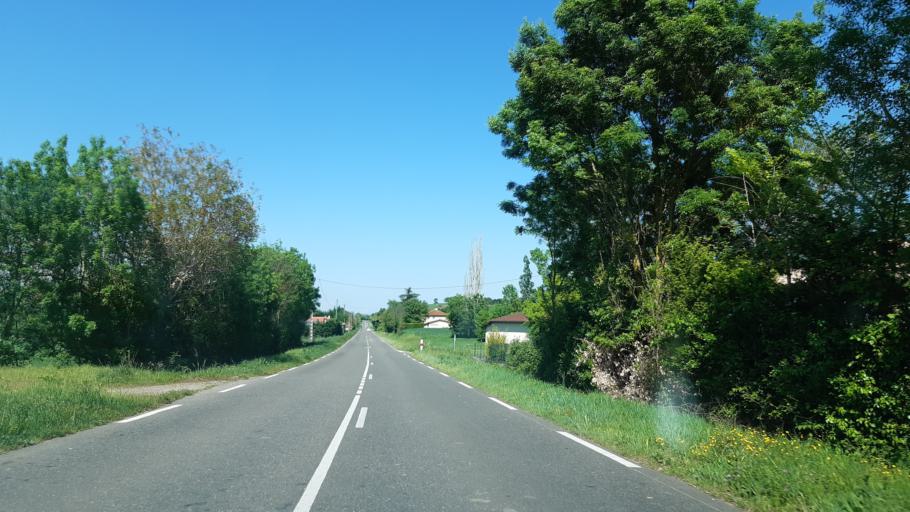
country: FR
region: Midi-Pyrenees
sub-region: Departement du Gers
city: Pujaudran
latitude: 43.5830
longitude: 1.0470
